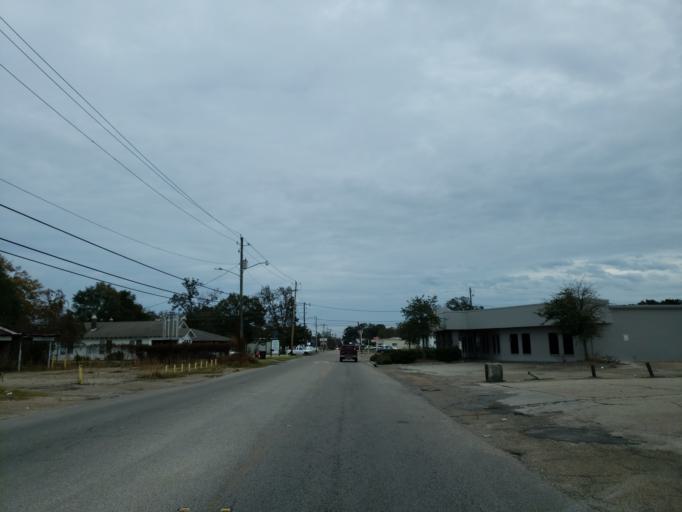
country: US
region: Mississippi
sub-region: Forrest County
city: Hattiesburg
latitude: 31.3140
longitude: -89.3049
